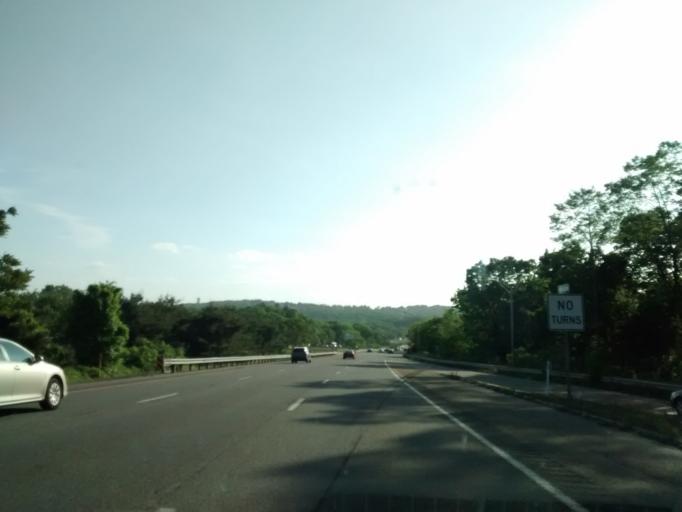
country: US
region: Massachusetts
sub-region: Worcester County
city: Shrewsbury
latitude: 42.2958
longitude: -71.7489
